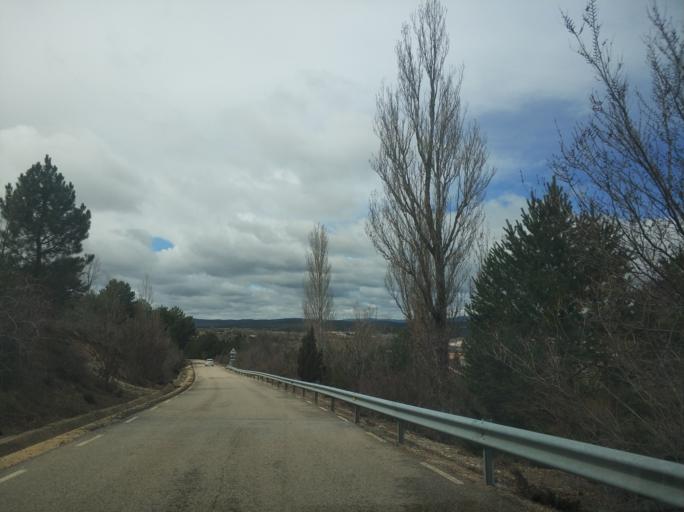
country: ES
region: Castille and Leon
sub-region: Provincia de Soria
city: Abejar
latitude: 41.7974
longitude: -2.7740
